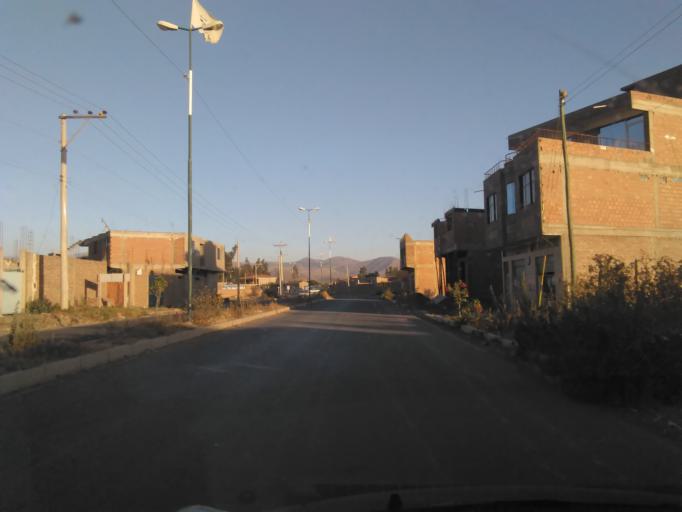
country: BO
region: Cochabamba
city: Punata
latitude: -17.5473
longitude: -65.8258
